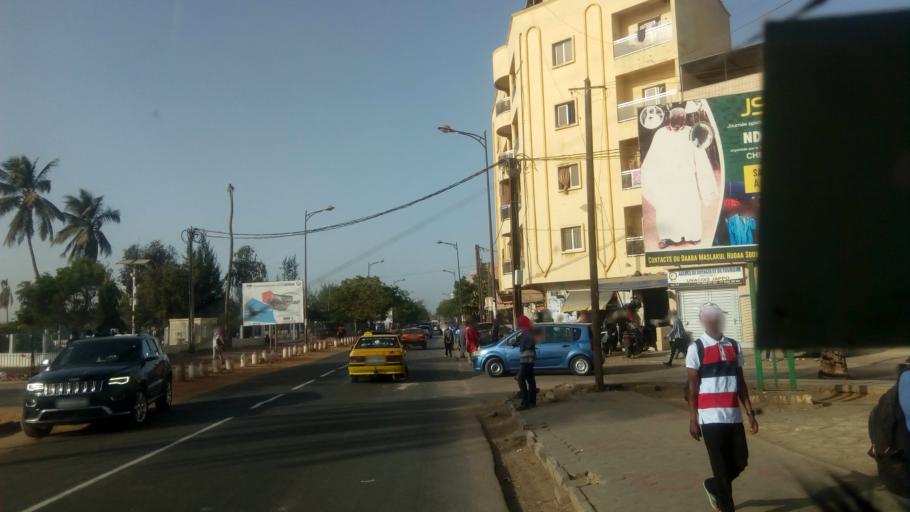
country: SN
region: Dakar
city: Dakar
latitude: 14.6936
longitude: -17.4476
